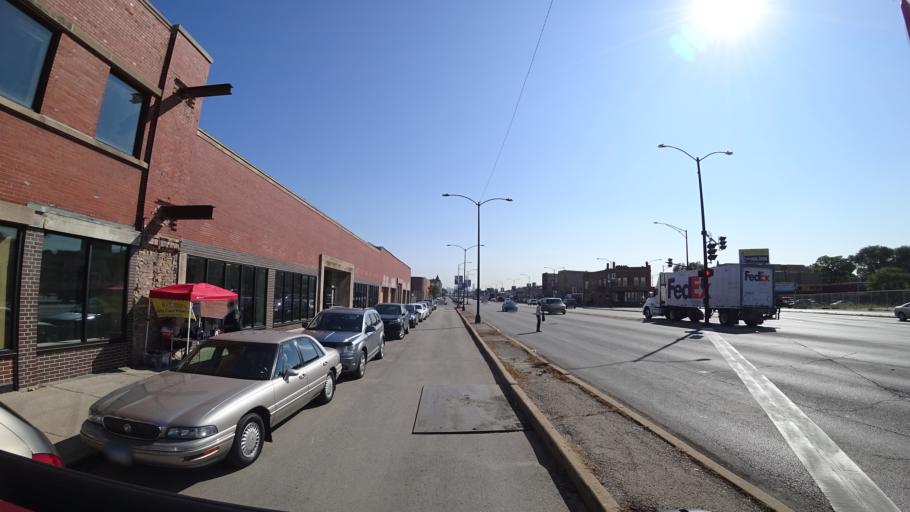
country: US
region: Illinois
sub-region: Cook County
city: Cicero
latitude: 41.8518
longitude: -87.7233
